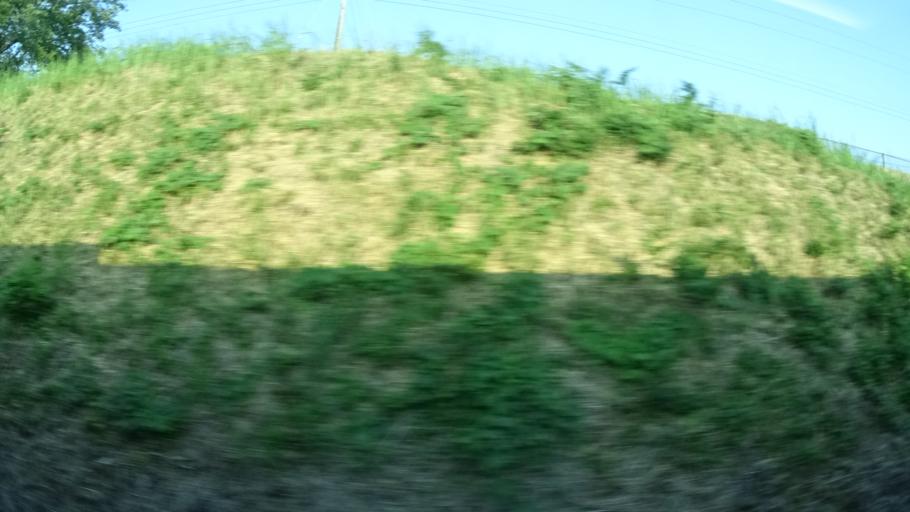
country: JP
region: Ibaraki
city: Funaishikawa
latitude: 36.4383
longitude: 140.5436
